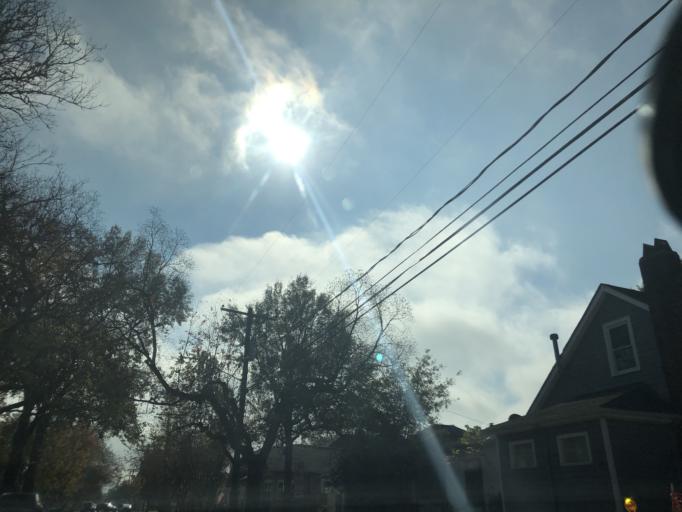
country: US
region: Louisiana
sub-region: Jefferson Parish
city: Metairie
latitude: 29.9821
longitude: -90.1527
